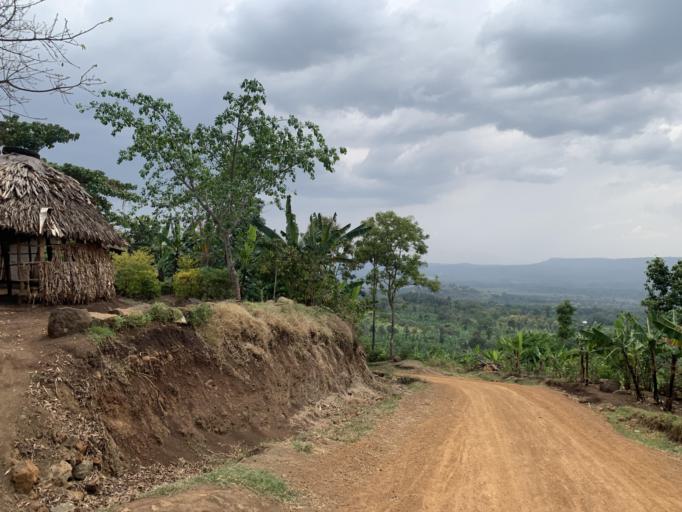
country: UG
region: Eastern Region
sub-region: Sironko District
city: Sironko
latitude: 1.2607
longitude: 34.2913
